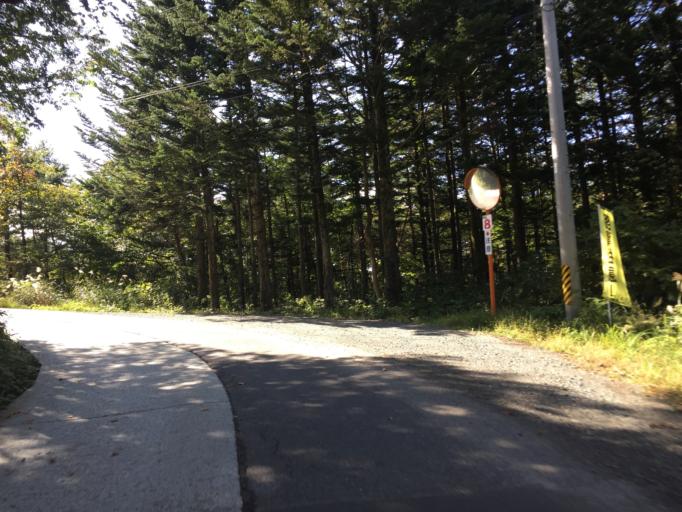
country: JP
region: Yamagata
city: Yonezawa
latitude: 37.8050
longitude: 140.2780
